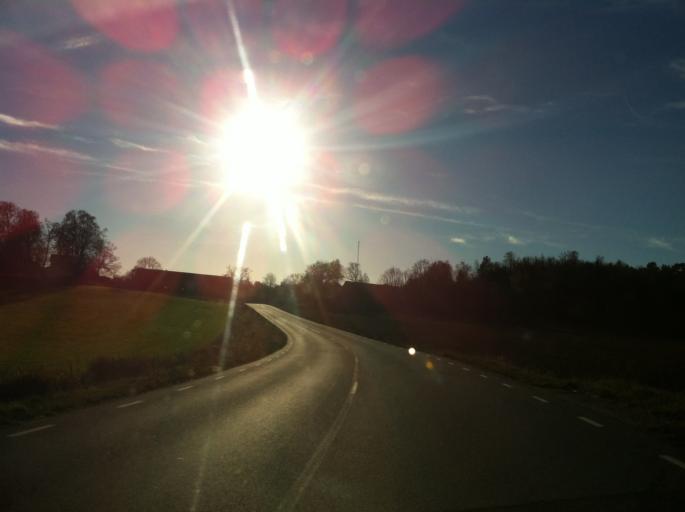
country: SE
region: Blekinge
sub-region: Karlshamns Kommun
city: Karlshamn
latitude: 56.1982
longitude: 14.9308
